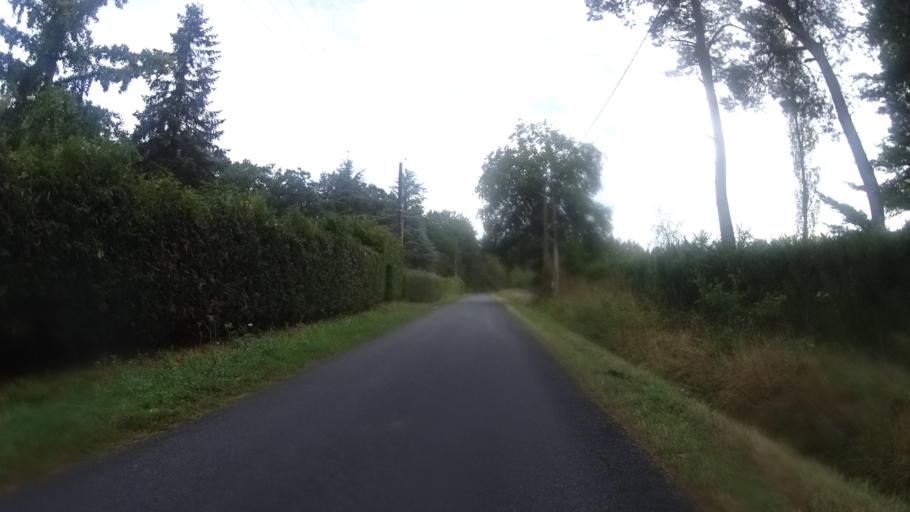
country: FR
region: Centre
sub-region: Departement du Loiret
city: Fay-aux-Loges
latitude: 47.9265
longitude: 2.1957
